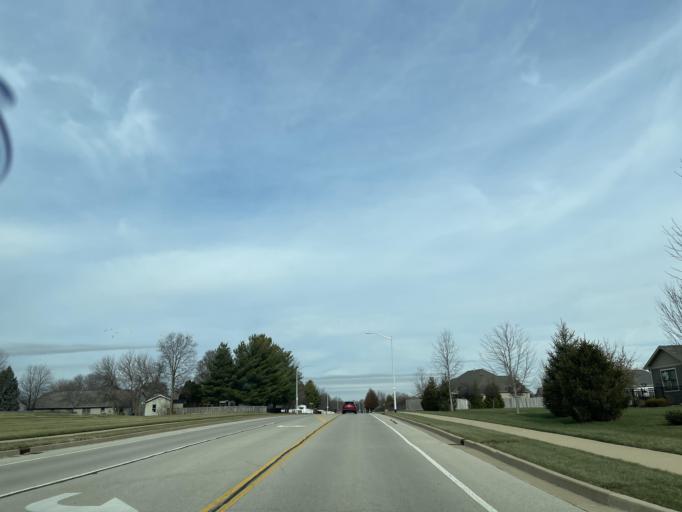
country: US
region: Illinois
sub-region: Sangamon County
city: Jerome
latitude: 39.7737
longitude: -89.7298
